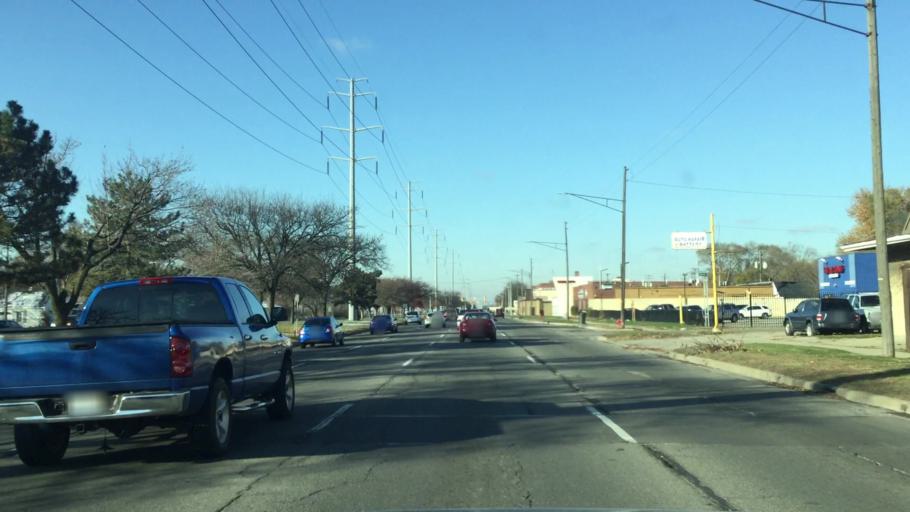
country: US
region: Michigan
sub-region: Macomb County
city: Warren
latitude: 42.4484
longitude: -83.0288
